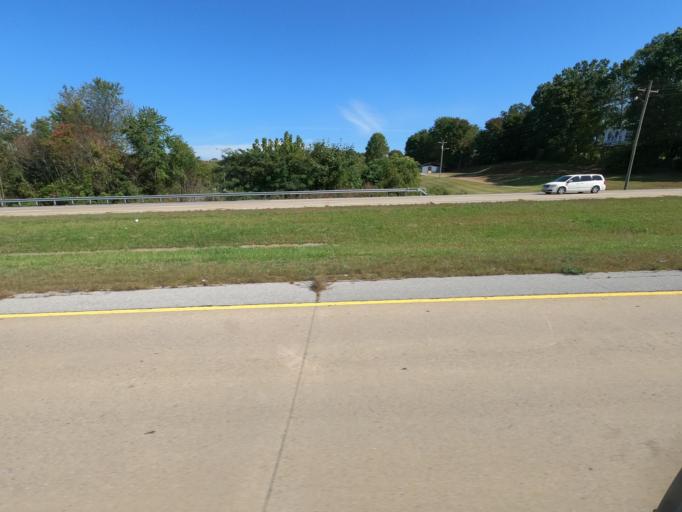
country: US
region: Tennessee
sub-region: Hamblen County
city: Morristown
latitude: 36.2483
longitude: -83.2723
